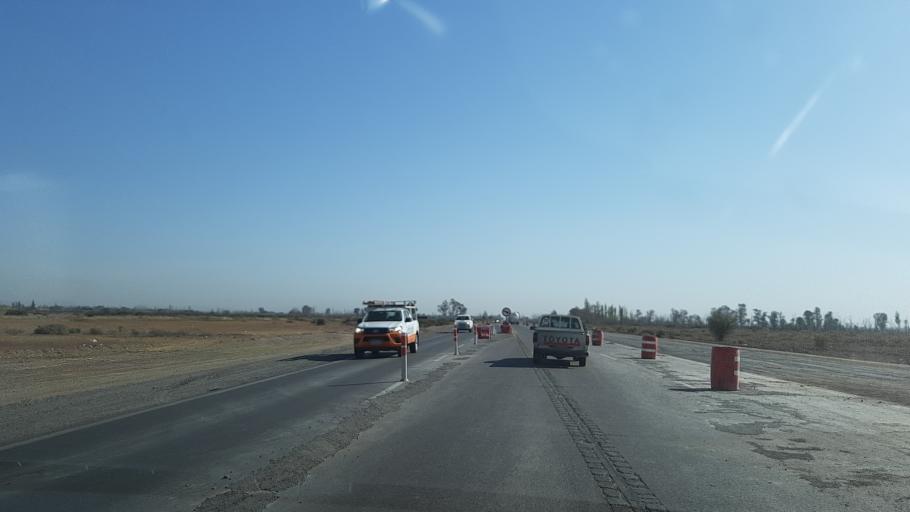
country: AR
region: San Juan
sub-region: Departamento de Pocito
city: Pocito
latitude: -31.7199
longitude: -68.5565
